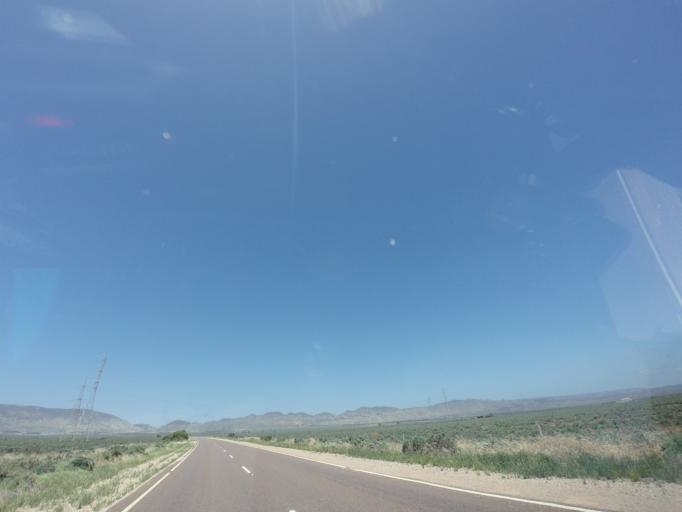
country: AU
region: South Australia
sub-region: Port Augusta
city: Port Augusta
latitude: -32.6260
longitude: 137.9415
